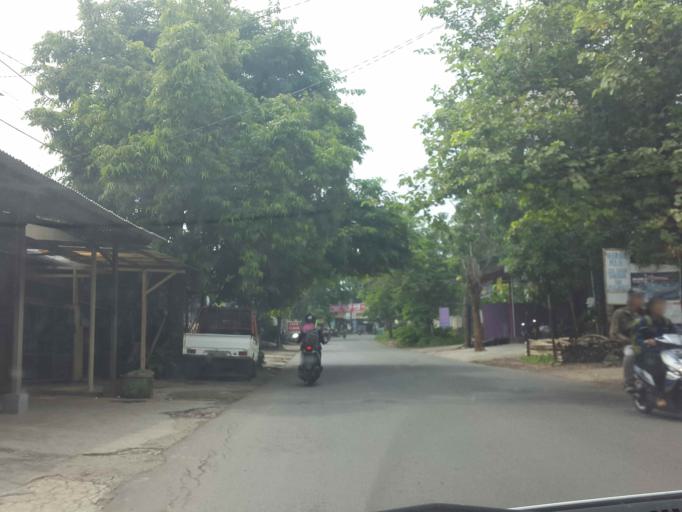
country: ID
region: Central Java
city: Semarang
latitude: -7.0607
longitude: 110.4453
